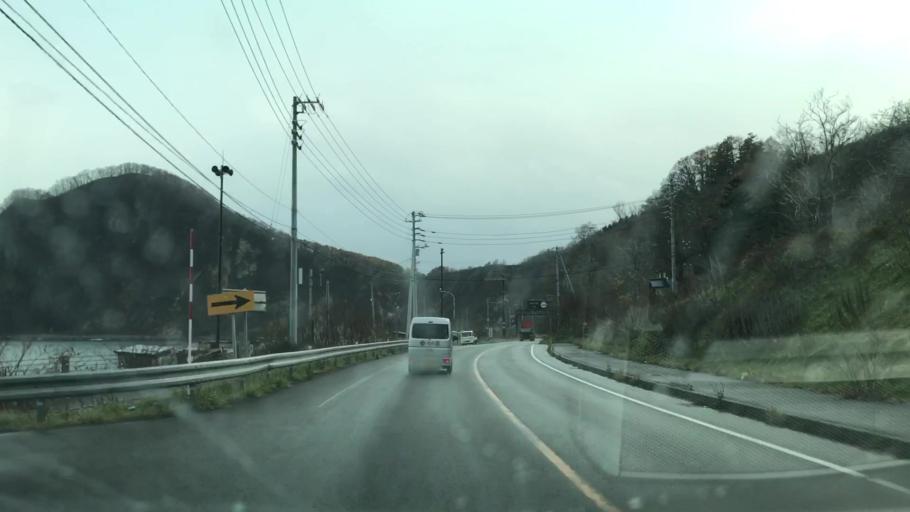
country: JP
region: Hokkaido
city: Yoichi
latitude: 43.2921
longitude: 140.6314
